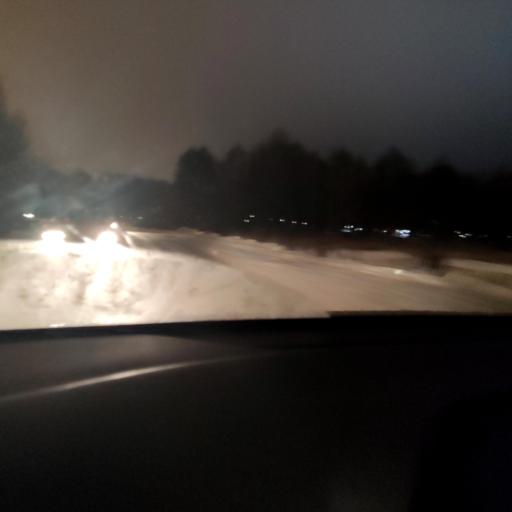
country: RU
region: Tatarstan
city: Osinovo
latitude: 55.8966
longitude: 48.8909
